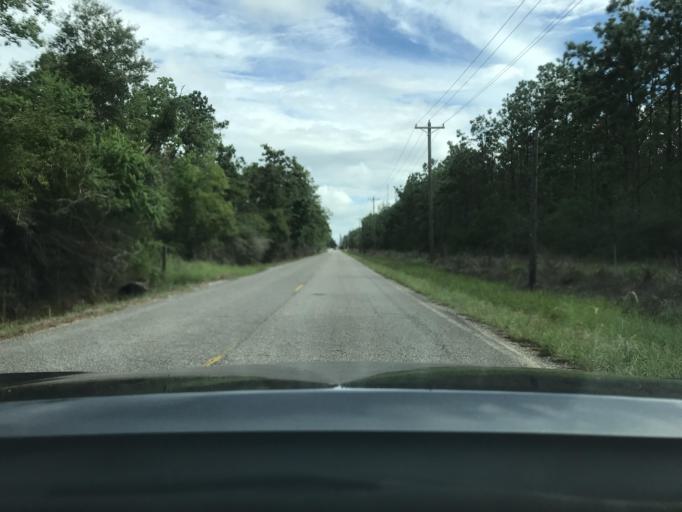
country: US
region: Louisiana
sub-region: Calcasieu Parish
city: Westlake
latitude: 30.2678
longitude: -93.2751
